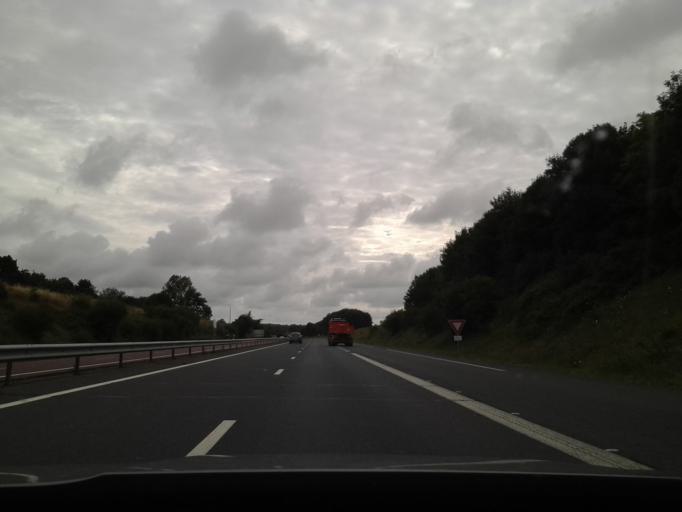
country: FR
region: Lower Normandy
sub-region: Departement du Calvados
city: Isigny-sur-Mer
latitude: 49.3314
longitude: -1.0703
